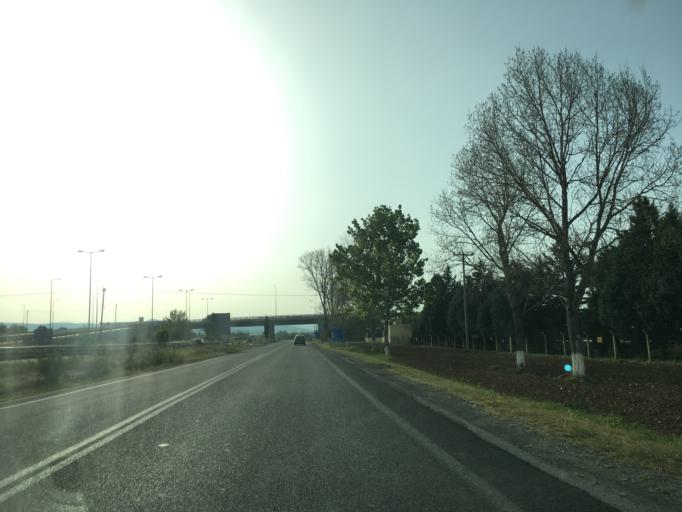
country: GR
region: Thessaly
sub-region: Nomos Magnisias
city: Velestino
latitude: 39.3879
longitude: 22.7769
